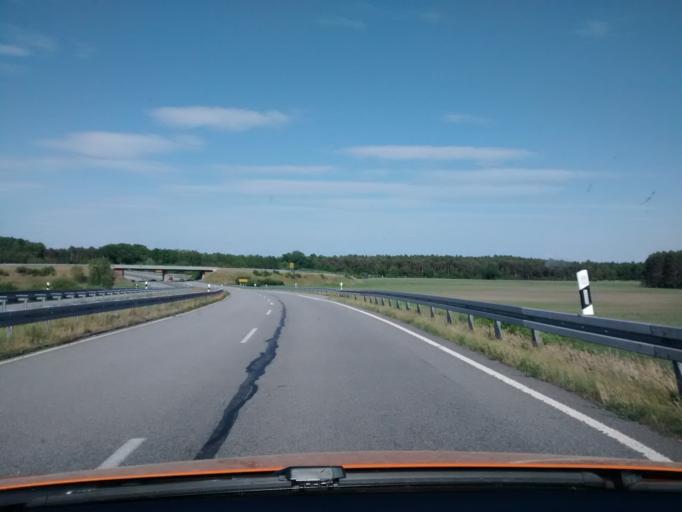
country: DE
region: Brandenburg
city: Luckenwalde
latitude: 52.1238
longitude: 13.2086
